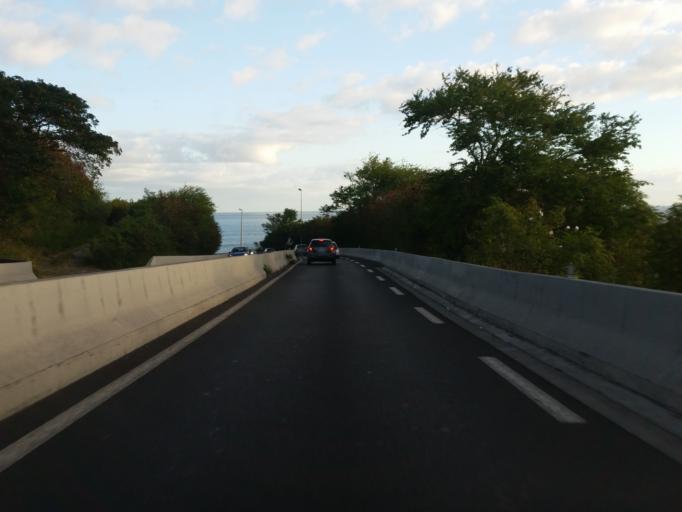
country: RE
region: Reunion
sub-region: Reunion
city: Saint-Denis
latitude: -20.8783
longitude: 55.4380
